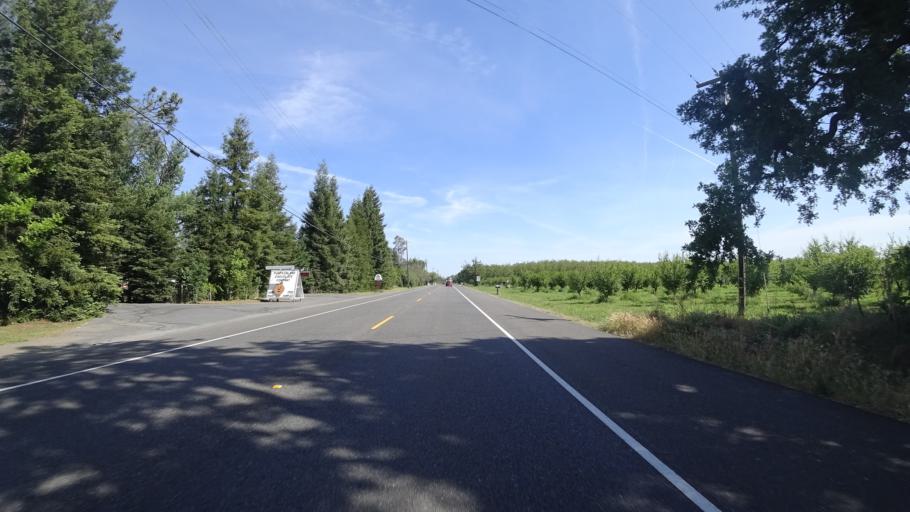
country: US
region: California
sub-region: Tehama County
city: Gerber
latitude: 40.1422
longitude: -122.1329
